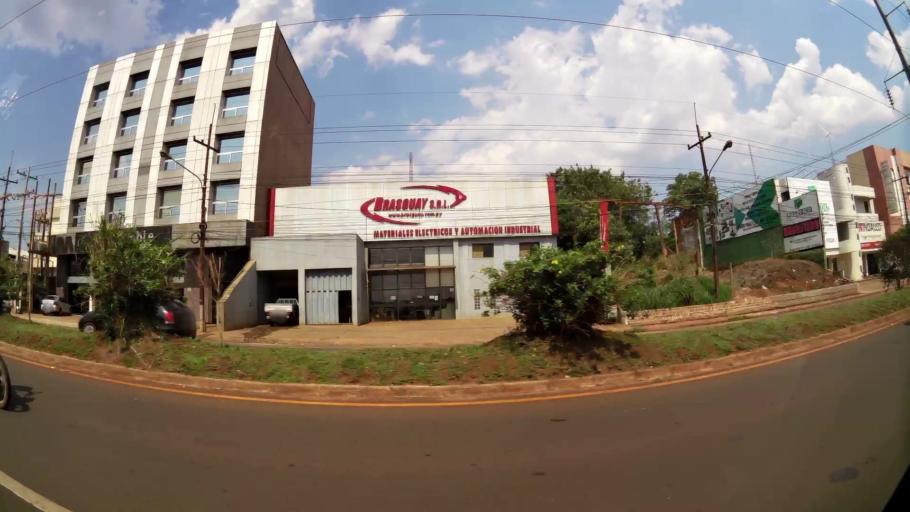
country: PY
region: Alto Parana
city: Ciudad del Este
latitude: -25.5010
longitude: -54.6362
